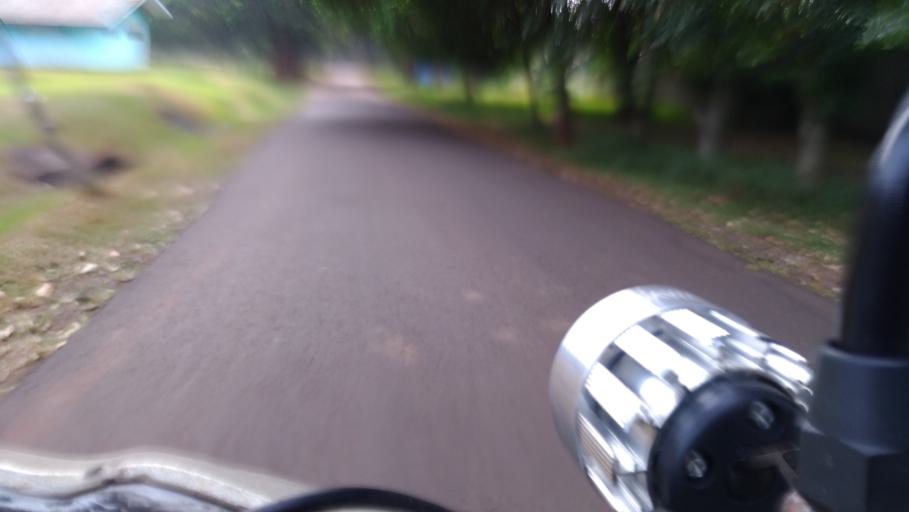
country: ID
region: West Java
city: Cileungsir
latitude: -6.3628
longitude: 106.8978
